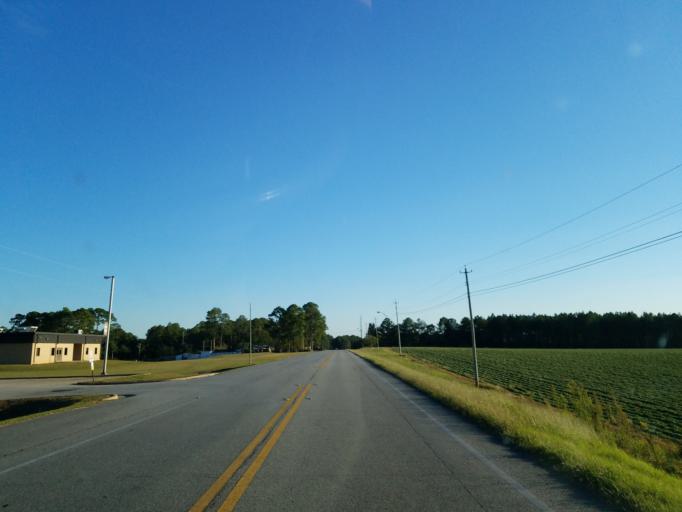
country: US
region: Georgia
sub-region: Worth County
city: Sylvester
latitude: 31.5474
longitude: -83.8431
